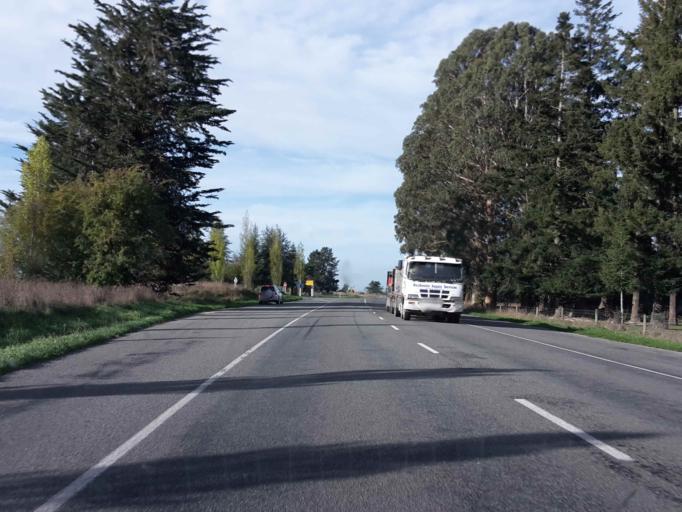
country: NZ
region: Canterbury
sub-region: Ashburton District
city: Tinwald
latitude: -44.0459
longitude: 171.4172
